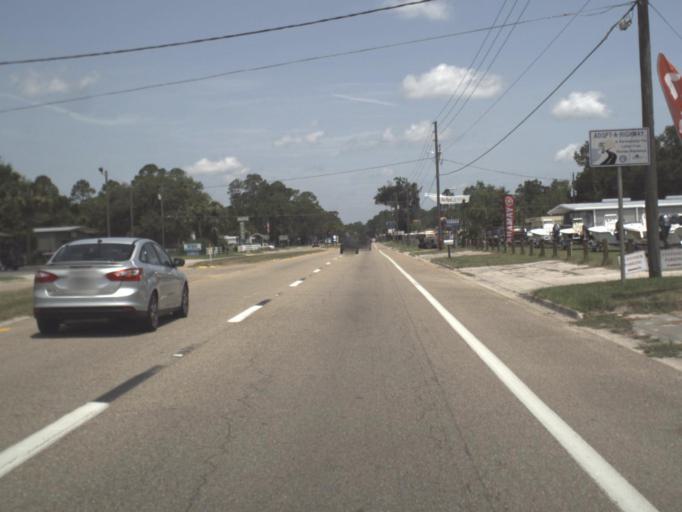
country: US
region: Florida
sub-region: Taylor County
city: Perry
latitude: 30.0742
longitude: -83.5626
